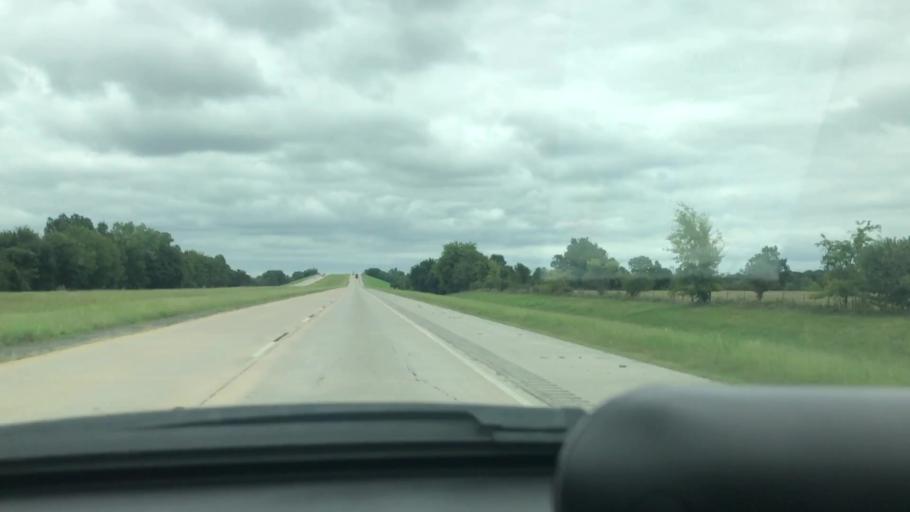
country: US
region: Oklahoma
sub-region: Wagoner County
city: Wagoner
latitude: 35.8754
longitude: -95.4021
